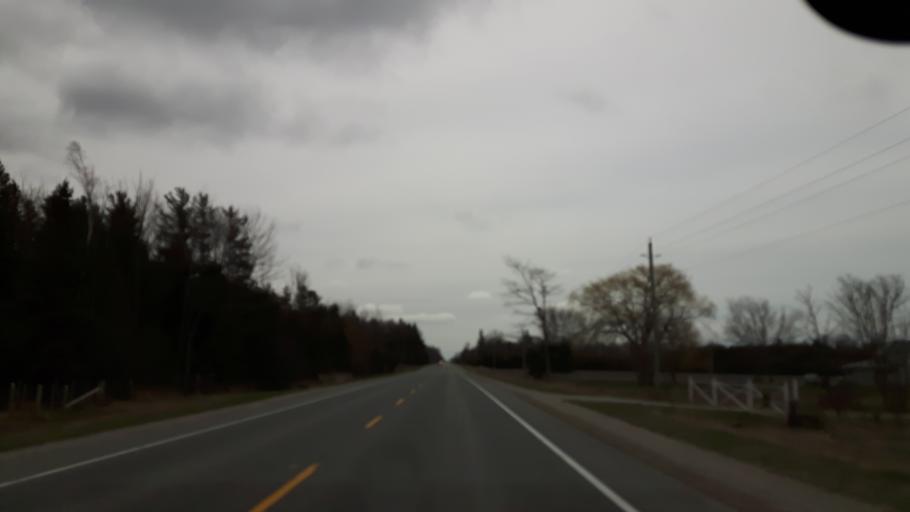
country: CA
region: Ontario
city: Goderich
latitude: 43.6727
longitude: -81.7057
